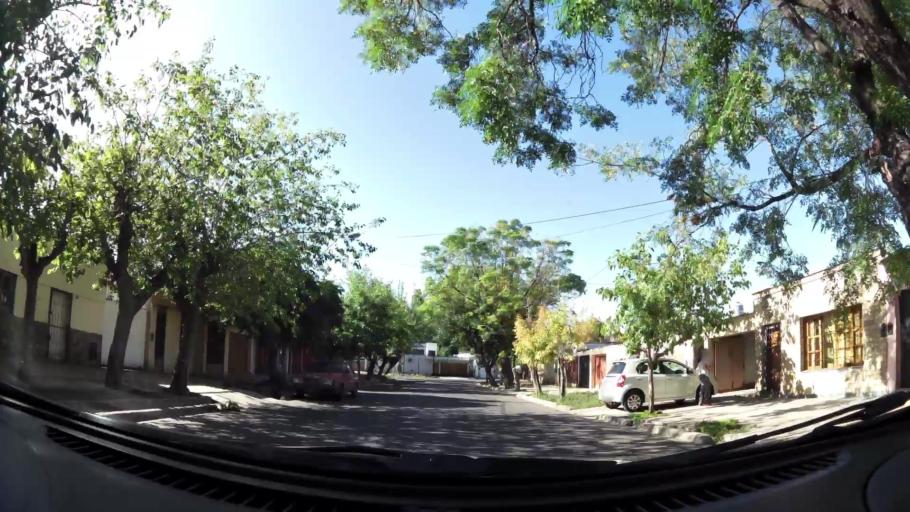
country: AR
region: Mendoza
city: Mendoza
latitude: -32.8994
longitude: -68.8179
